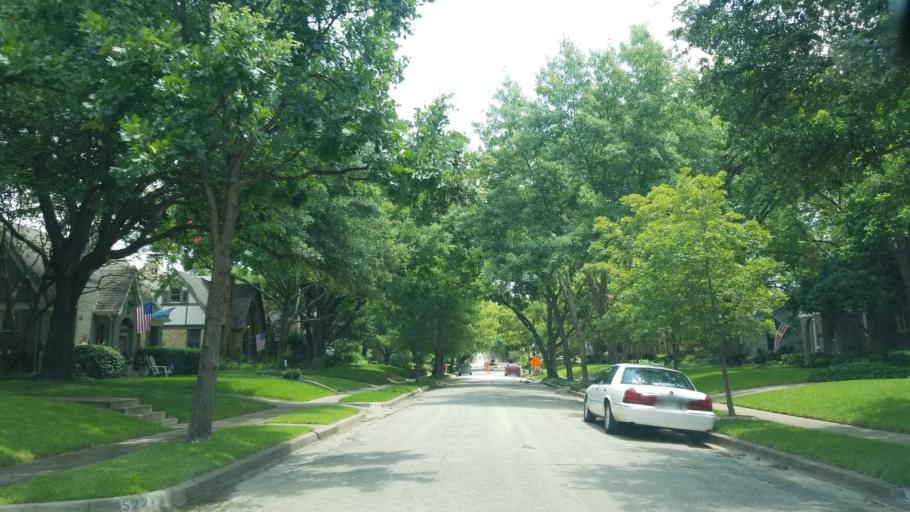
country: US
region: Texas
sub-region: Dallas County
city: Highland Park
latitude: 32.8273
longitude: -96.7810
